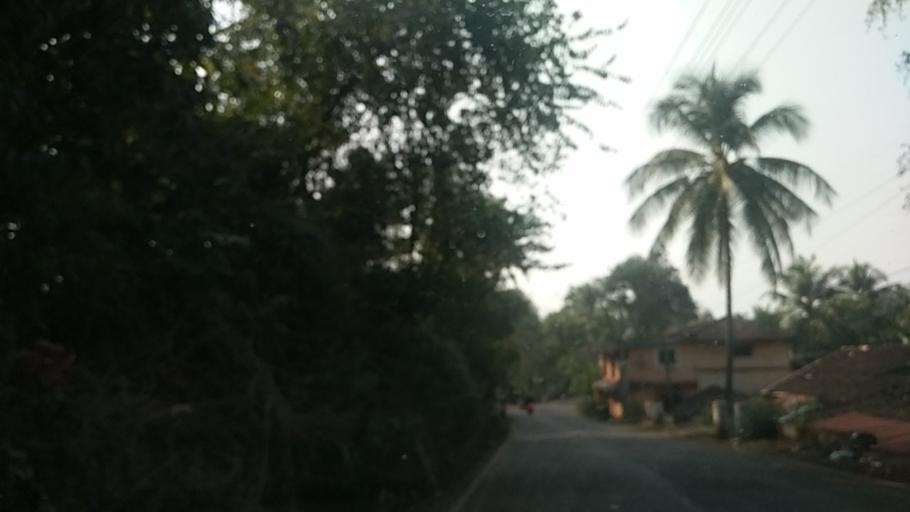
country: IN
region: Goa
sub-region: North Goa
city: Pernem
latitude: 15.7166
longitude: 73.8009
